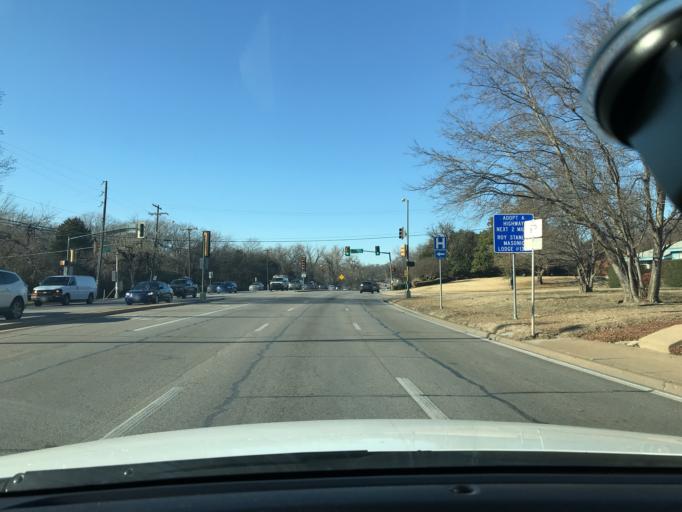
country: US
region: Texas
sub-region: Dallas County
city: Highland Park
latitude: 32.8352
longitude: -96.7039
